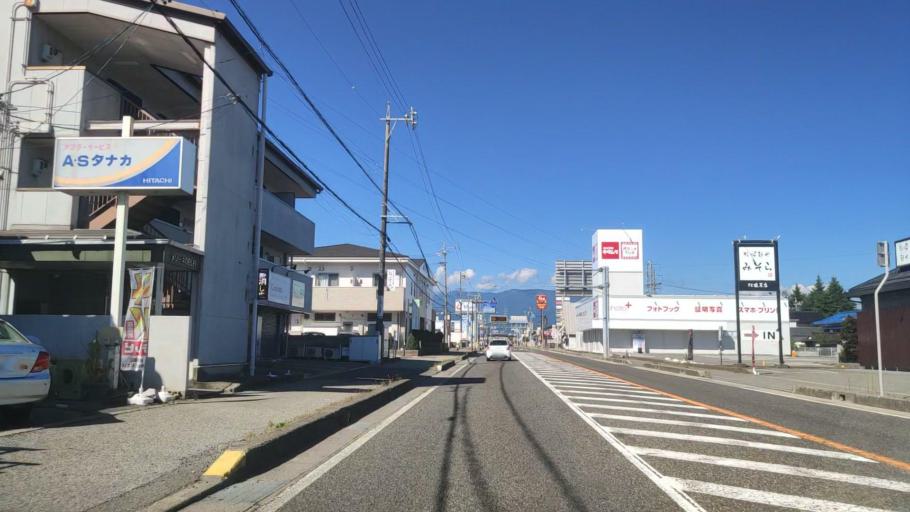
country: JP
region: Nagano
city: Shiojiri
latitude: 36.1191
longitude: 137.9563
